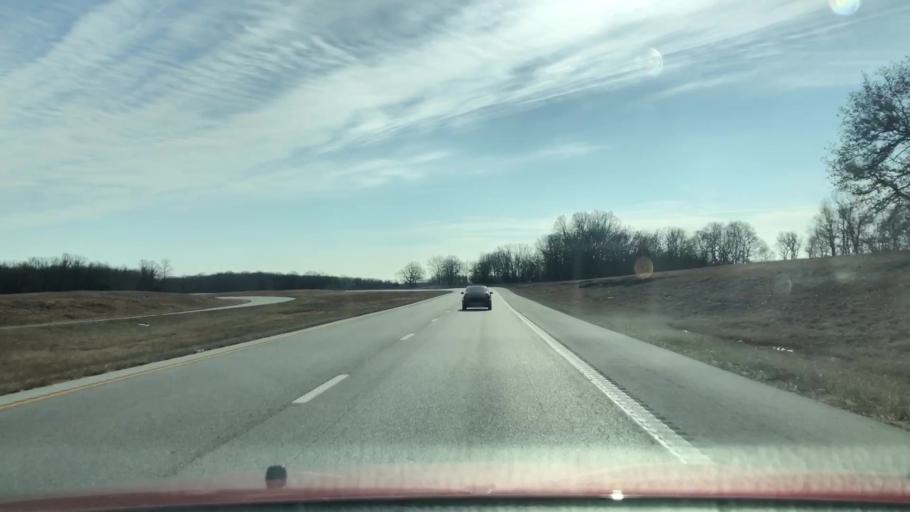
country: US
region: Missouri
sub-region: Webster County
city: Seymour
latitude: 37.1338
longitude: -92.7431
